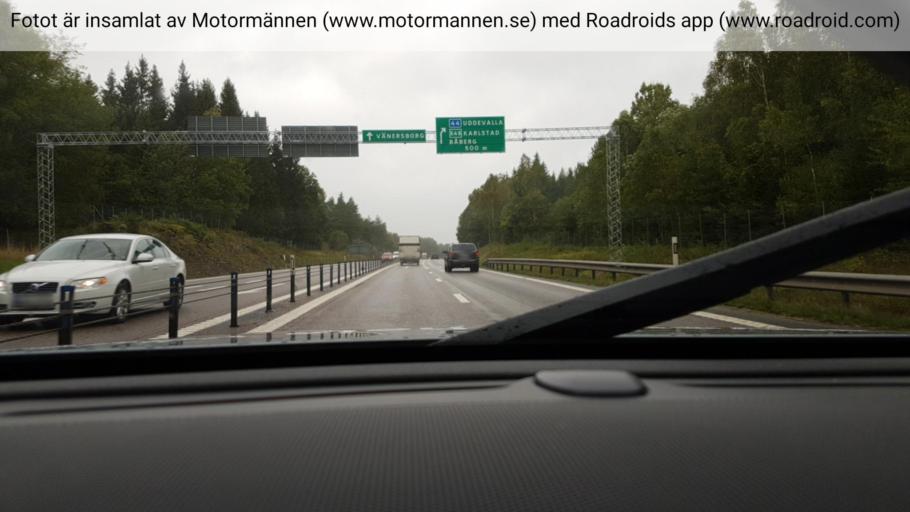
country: SE
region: Vaestra Goetaland
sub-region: Trollhattan
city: Trollhattan
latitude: 58.3244
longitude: 12.2996
